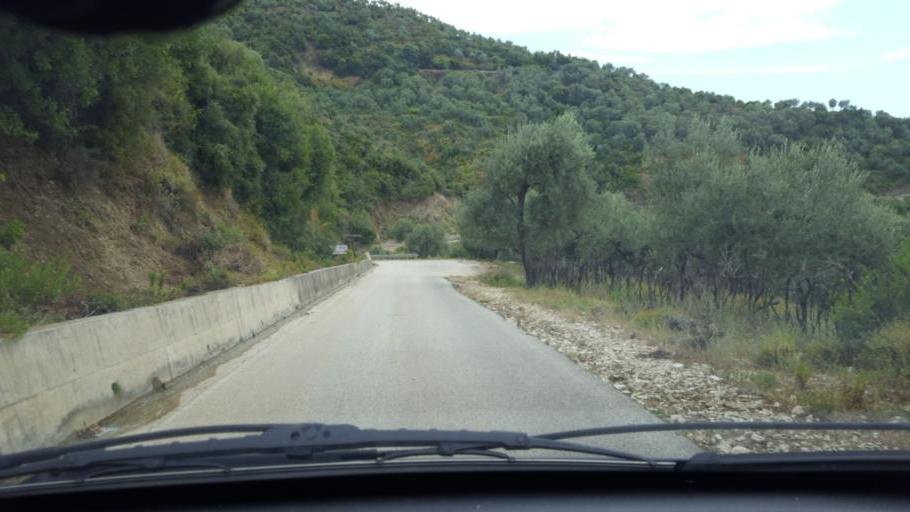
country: AL
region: Vlore
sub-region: Rrethi i Sarandes
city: Lukove
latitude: 39.9865
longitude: 19.9159
